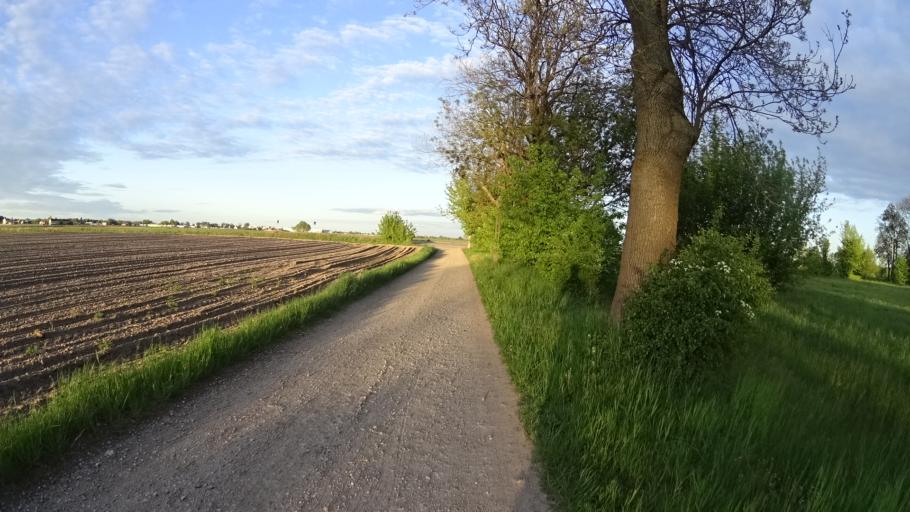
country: PL
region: Masovian Voivodeship
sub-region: Powiat warszawski zachodni
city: Jozefow
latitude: 52.2002
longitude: 20.7426
